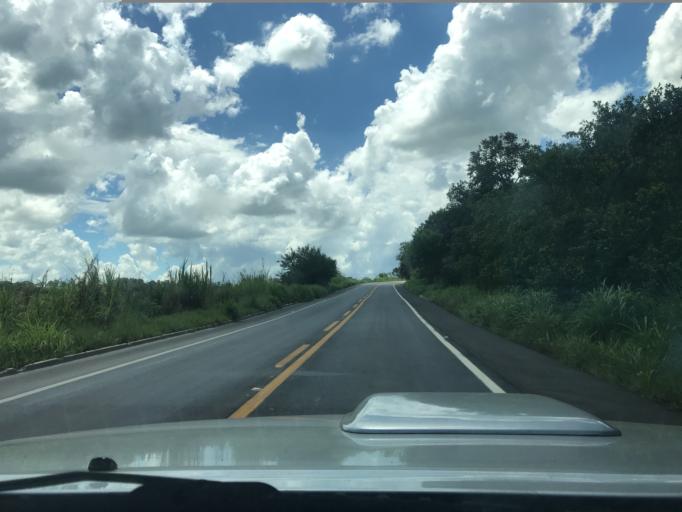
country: BR
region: Minas Gerais
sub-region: Formiga
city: Formiga
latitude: -20.6425
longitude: -45.3632
